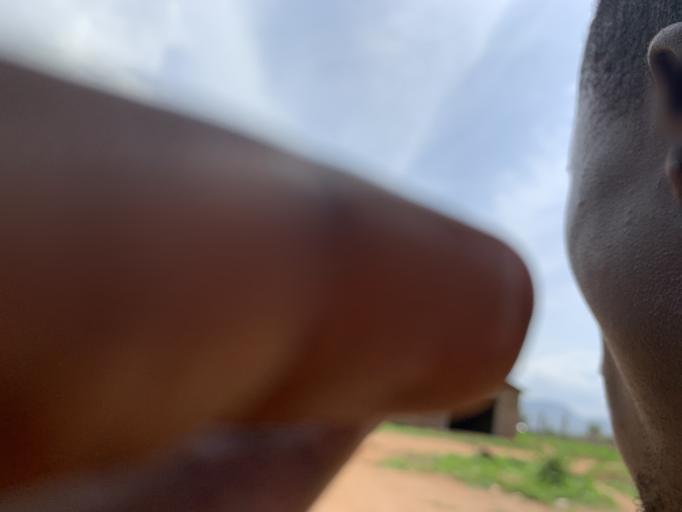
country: SL
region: Western Area
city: Waterloo
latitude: 8.3539
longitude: -13.0436
